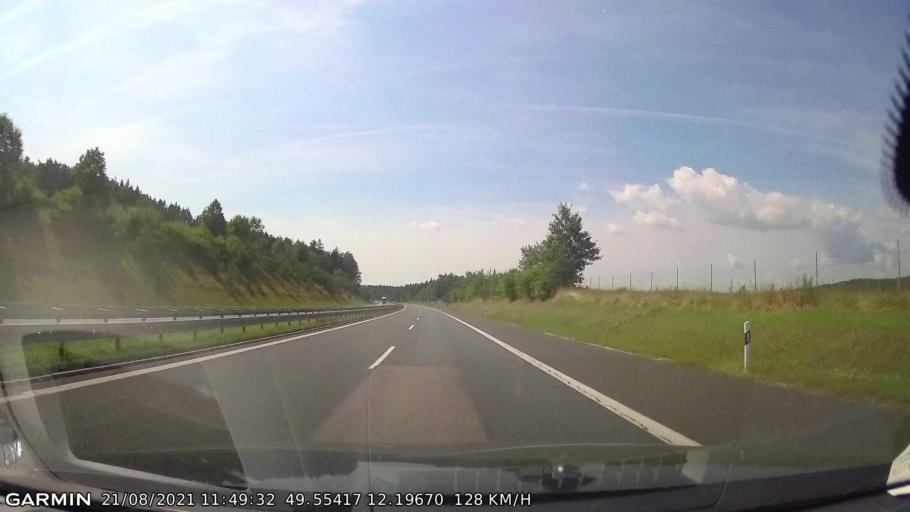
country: DE
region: Bavaria
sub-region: Upper Palatinate
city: Wernberg-Koblitz
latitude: 49.5539
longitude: 12.1964
